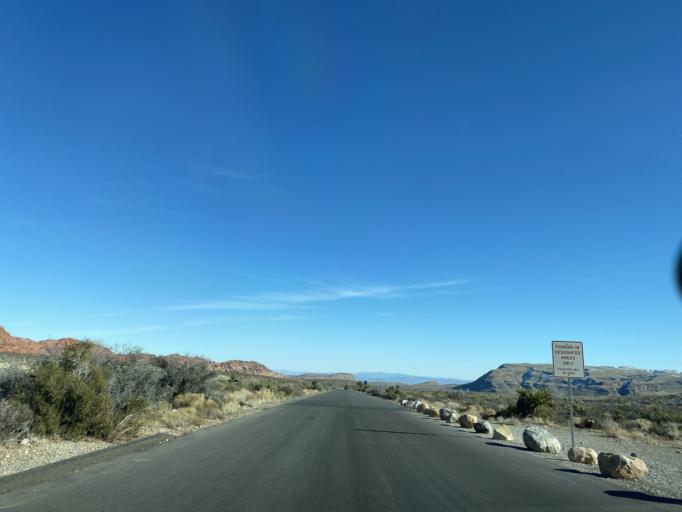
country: US
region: Nevada
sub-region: Clark County
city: Summerlin South
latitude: 36.1407
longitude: -115.4724
